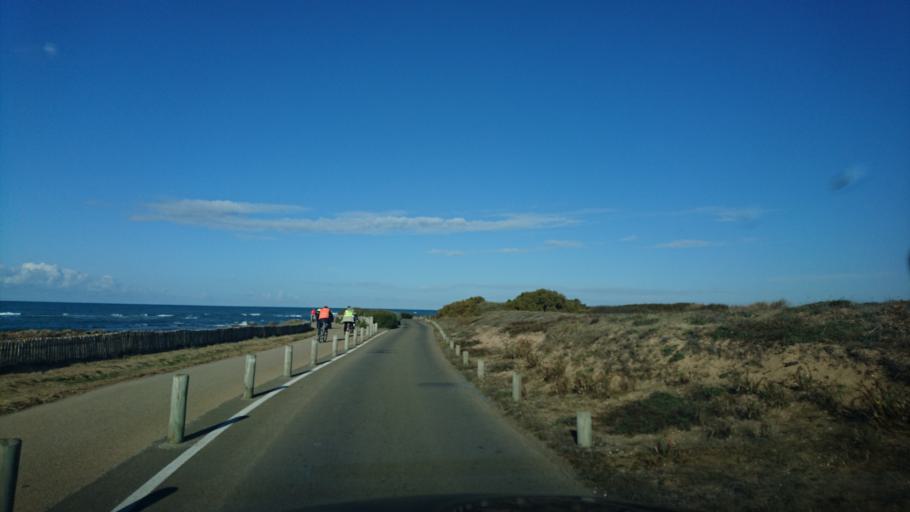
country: FR
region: Pays de la Loire
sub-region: Departement de la Vendee
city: Les Sables-d'Olonne
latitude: 46.5055
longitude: -1.8161
